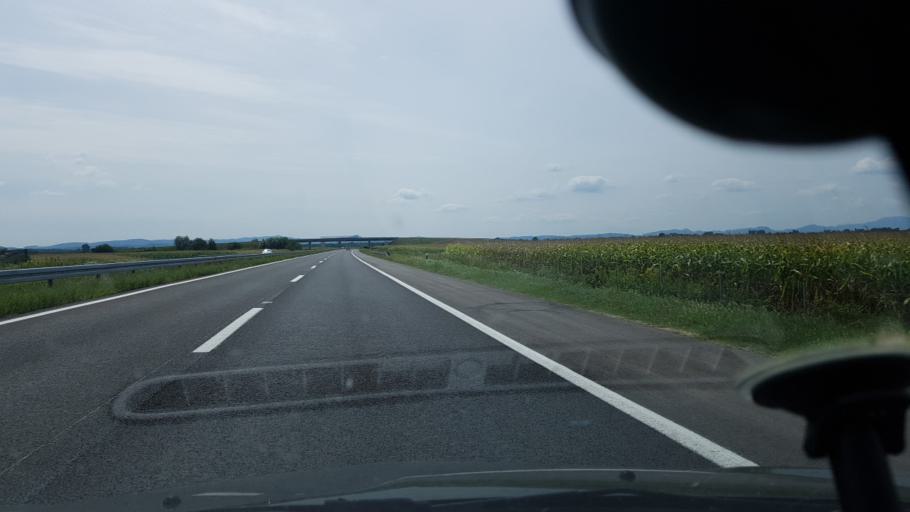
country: HR
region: Medimurska
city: Orehovica
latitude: 46.3444
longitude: 16.5313
